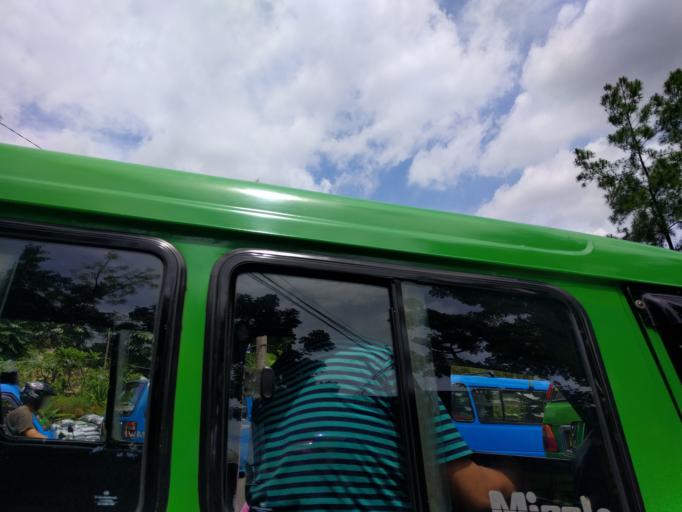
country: ID
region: West Java
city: Bogor
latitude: -6.6186
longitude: 106.8154
